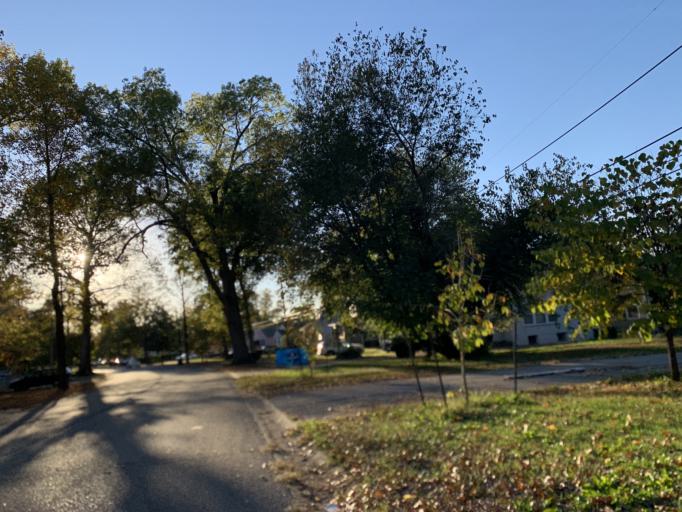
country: US
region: Indiana
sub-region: Floyd County
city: New Albany
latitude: 38.2741
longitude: -85.8137
